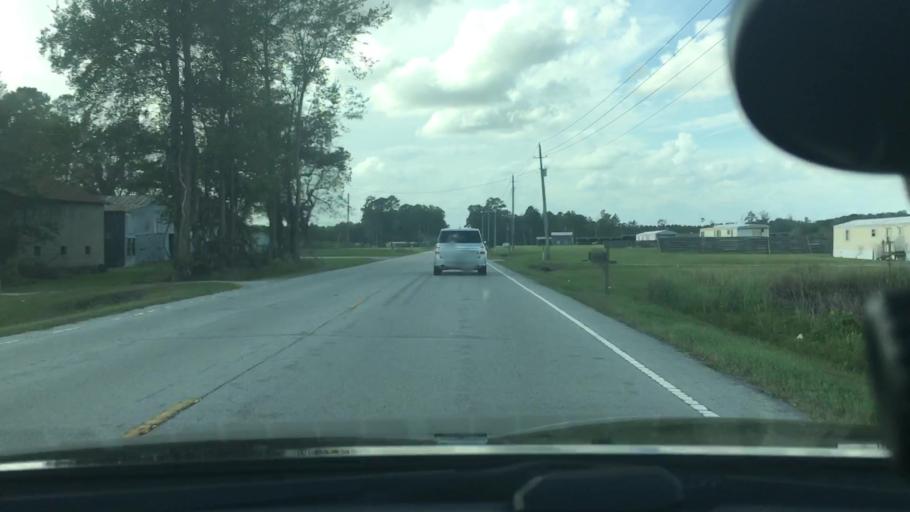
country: US
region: North Carolina
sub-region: Pitt County
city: Windsor
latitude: 35.4729
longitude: -77.2895
